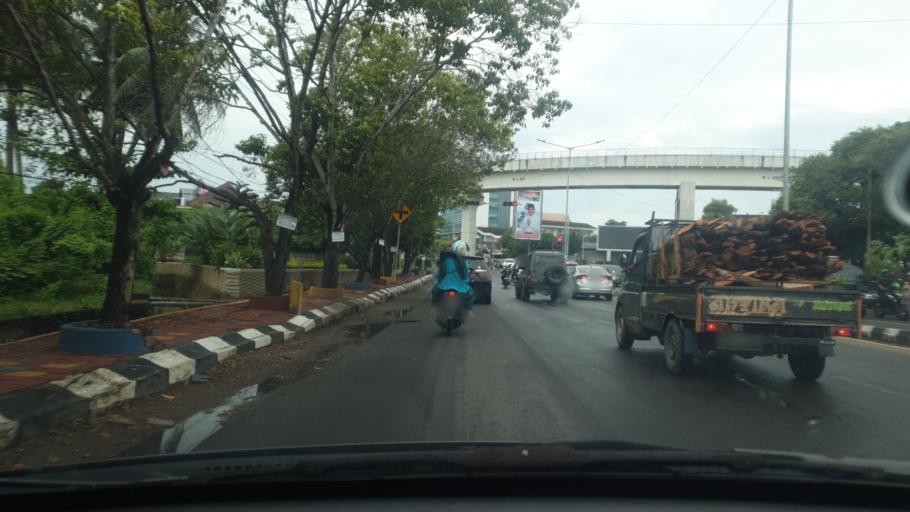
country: ID
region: South Sumatra
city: Palembang
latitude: -2.9697
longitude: 104.7325
